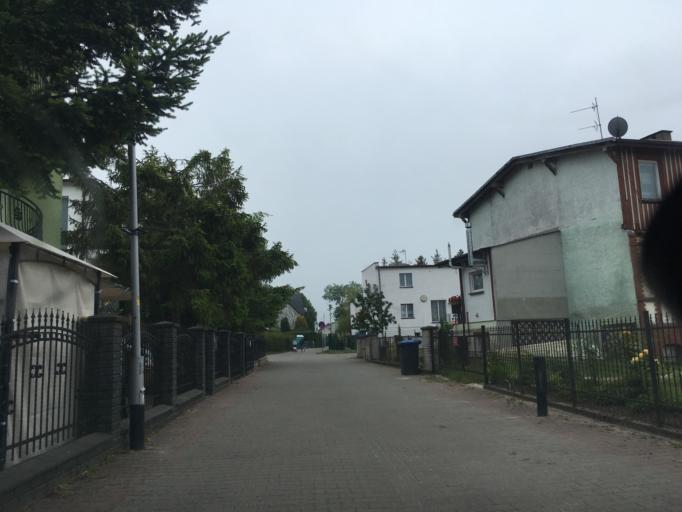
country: PL
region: West Pomeranian Voivodeship
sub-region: Powiat koszalinski
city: Mielno
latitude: 54.2684
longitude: 16.0840
